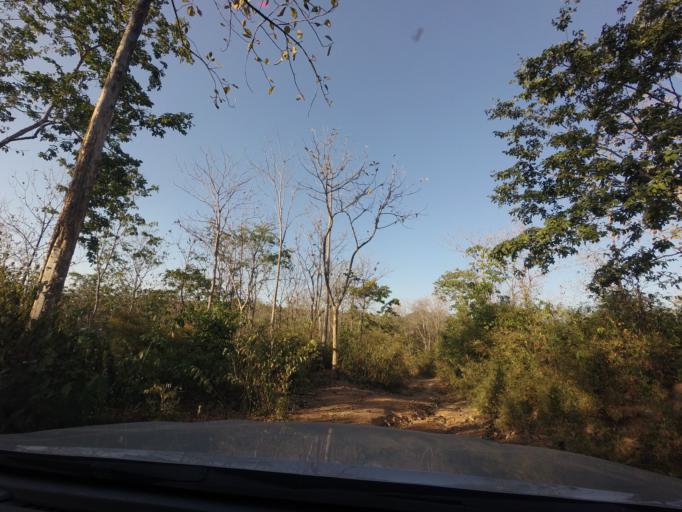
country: TH
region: Lampang
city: Mae Mo
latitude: 18.4166
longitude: 99.7385
